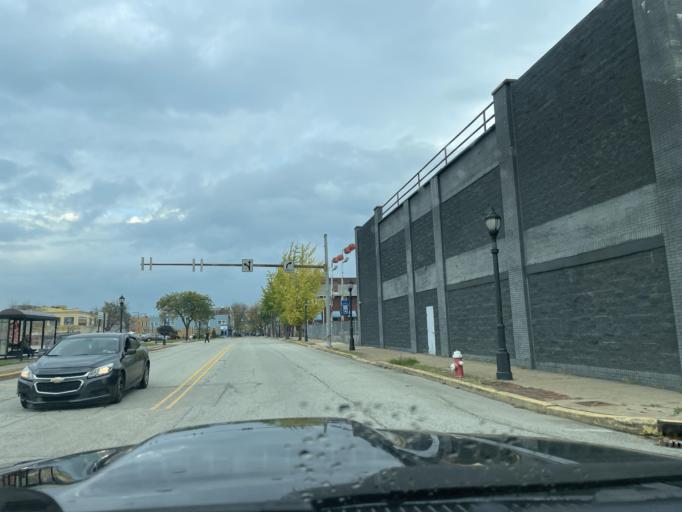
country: US
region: Pennsylvania
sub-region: Westmoreland County
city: New Kensington
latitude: 40.5638
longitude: -79.7659
